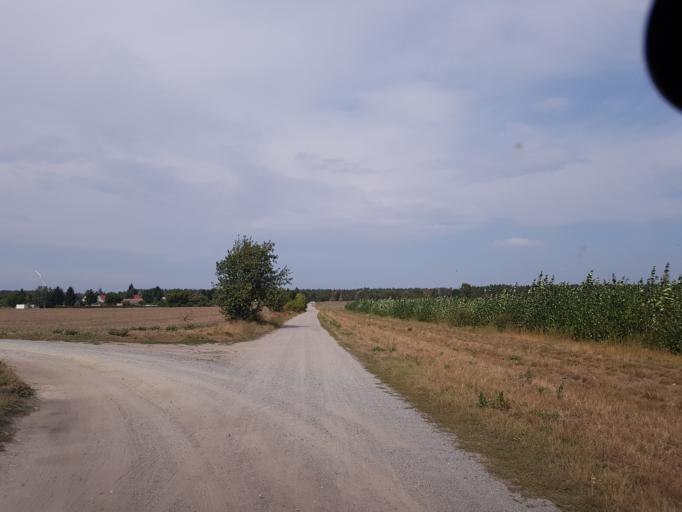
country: DE
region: Brandenburg
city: Finsterwalde
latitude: 51.6449
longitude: 13.7050
